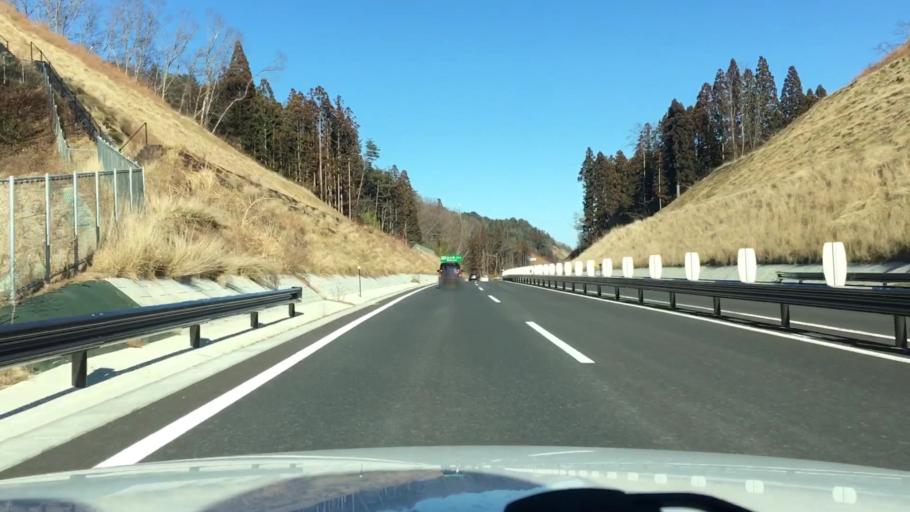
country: JP
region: Iwate
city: Miyako
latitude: 39.5776
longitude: 141.9293
